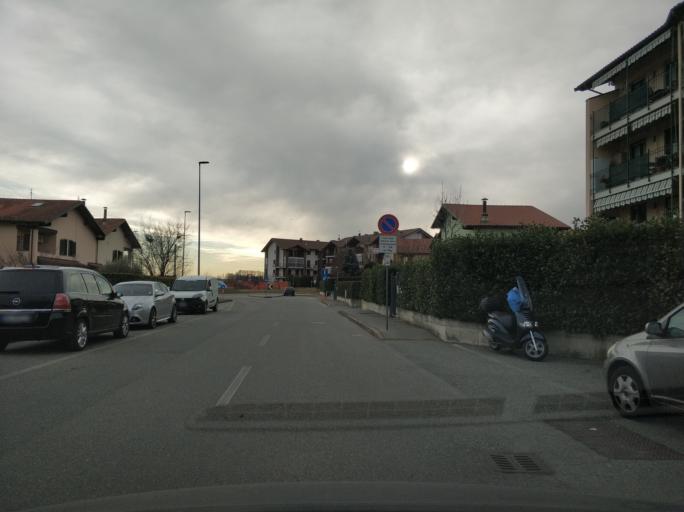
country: IT
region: Piedmont
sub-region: Provincia di Torino
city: San Maurizio
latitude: 45.2118
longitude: 7.6264
